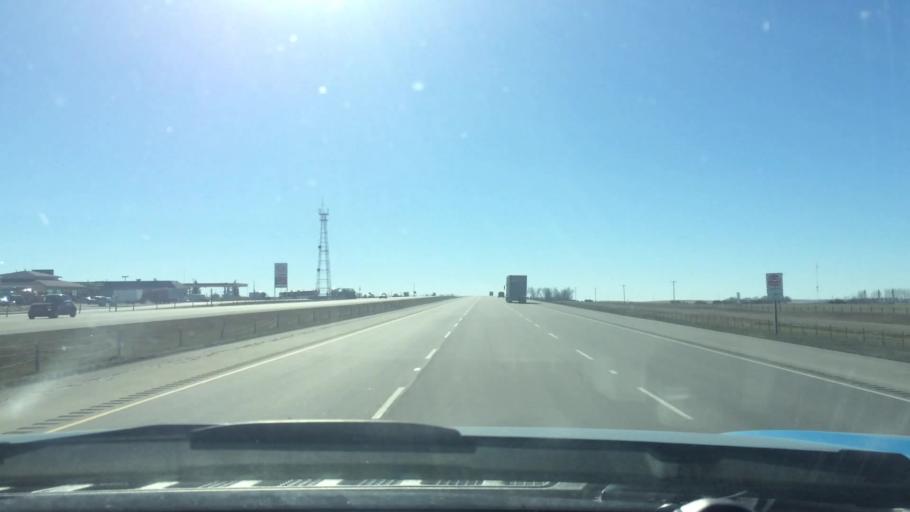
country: CA
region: Alberta
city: Crossfield
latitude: 51.4147
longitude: -114.0020
